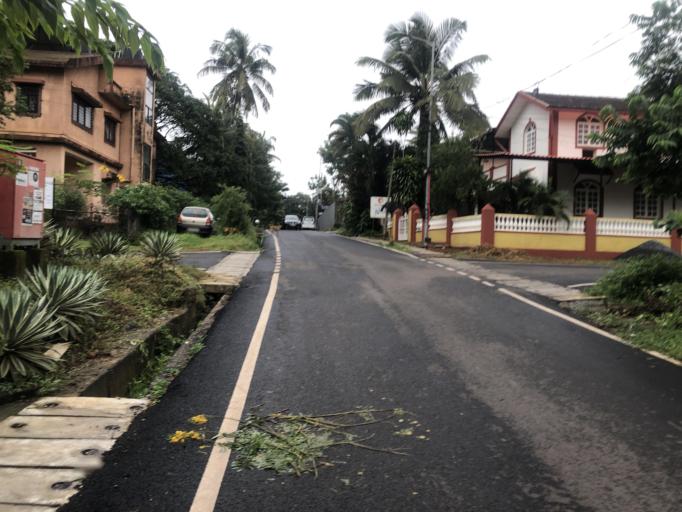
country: IN
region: Goa
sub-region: North Goa
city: Serula
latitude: 15.5360
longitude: 73.8280
